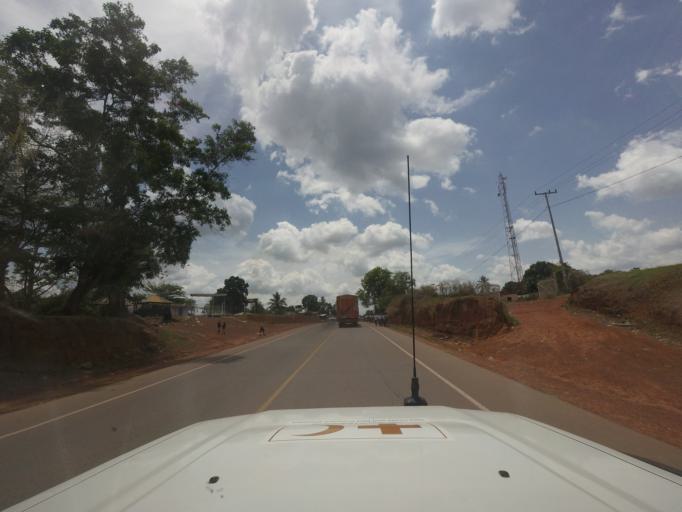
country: LR
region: Nimba
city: Sanniquellie
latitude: 7.2313
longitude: -8.9938
